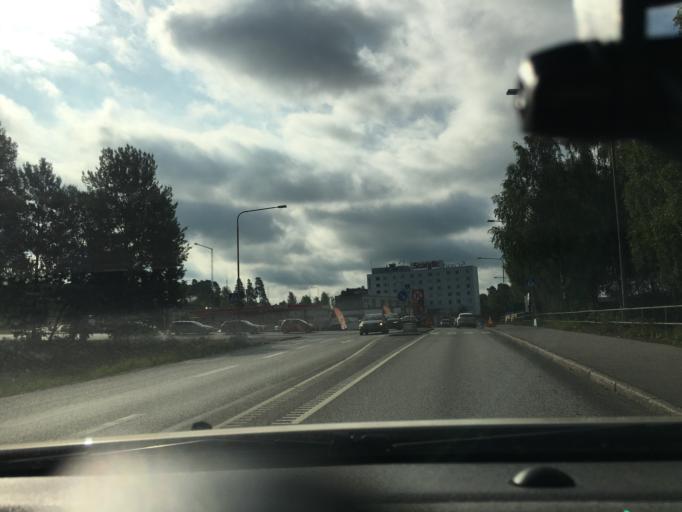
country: SE
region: Stockholm
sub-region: Sodertalje Kommun
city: Pershagen
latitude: 59.1758
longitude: 17.6409
